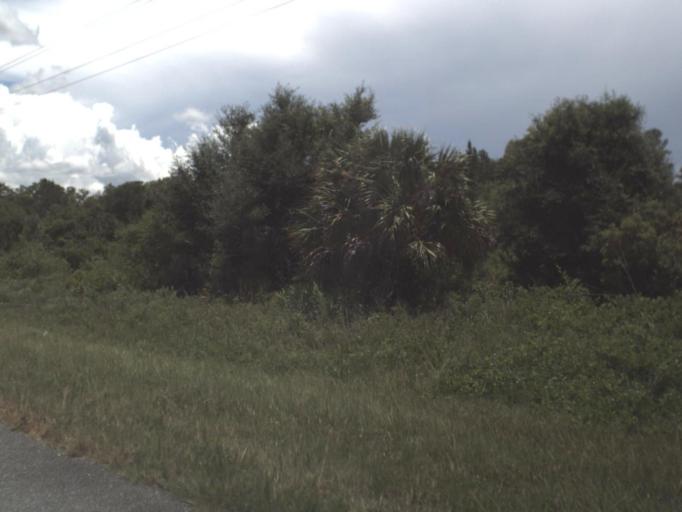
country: US
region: Florida
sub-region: Taylor County
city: Perry
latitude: 30.1428
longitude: -83.8607
